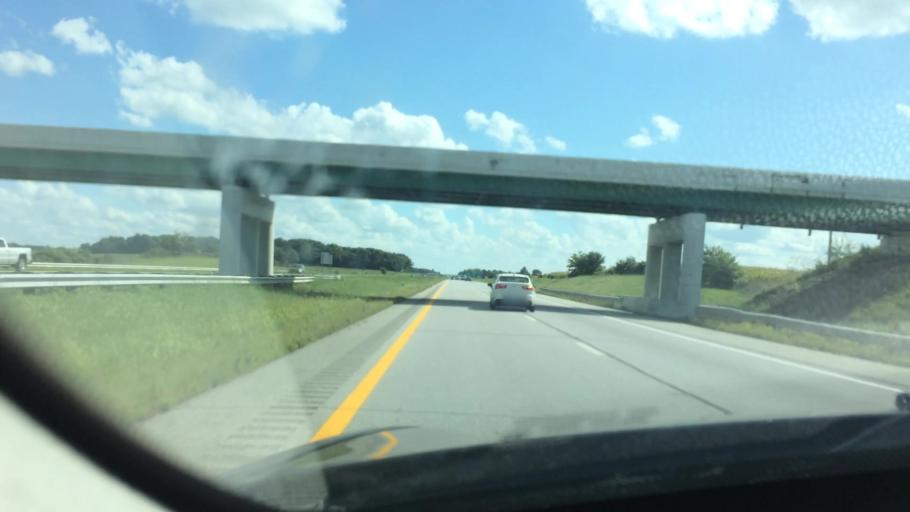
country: US
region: Ohio
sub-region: Shelby County
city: Botkins
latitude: 40.4531
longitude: -84.1701
